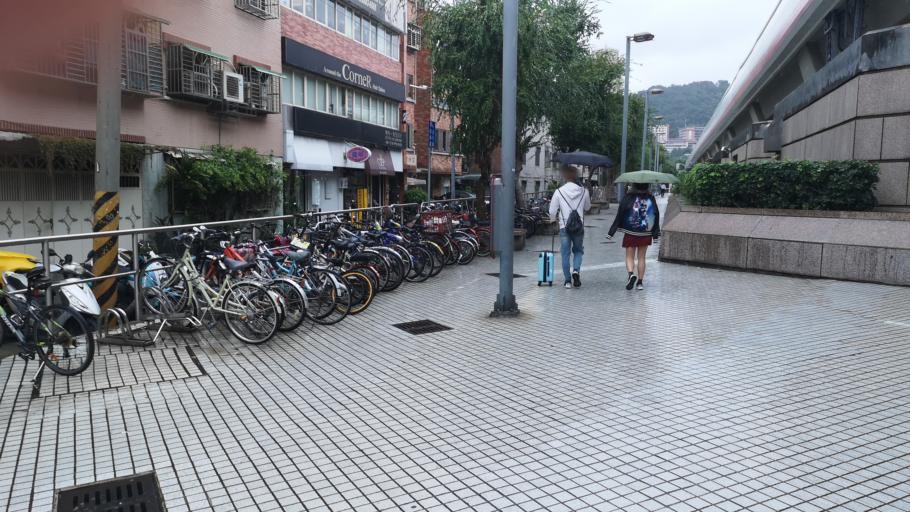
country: TW
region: Taipei
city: Taipei
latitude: 25.0941
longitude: 121.5263
